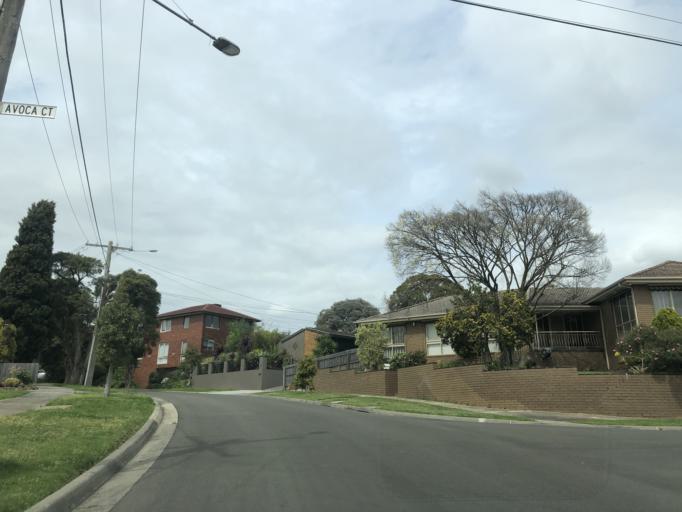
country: AU
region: Victoria
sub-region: Greater Dandenong
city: Noble Park North
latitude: -37.9416
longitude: 145.2115
